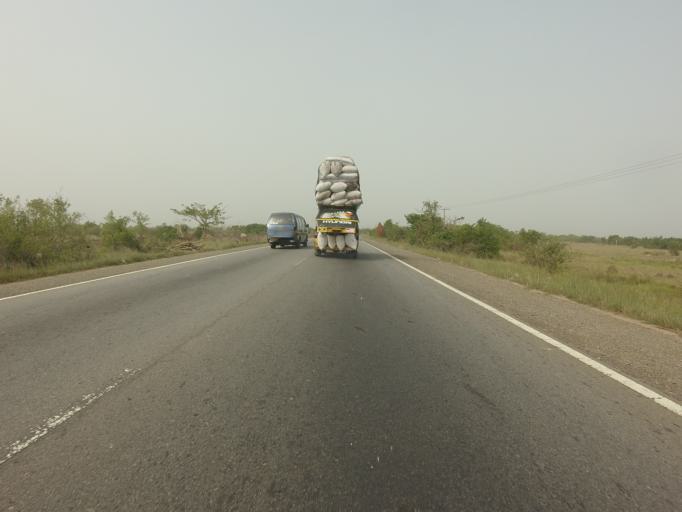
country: GH
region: Volta
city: Anloga
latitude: 5.9604
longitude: 0.5243
